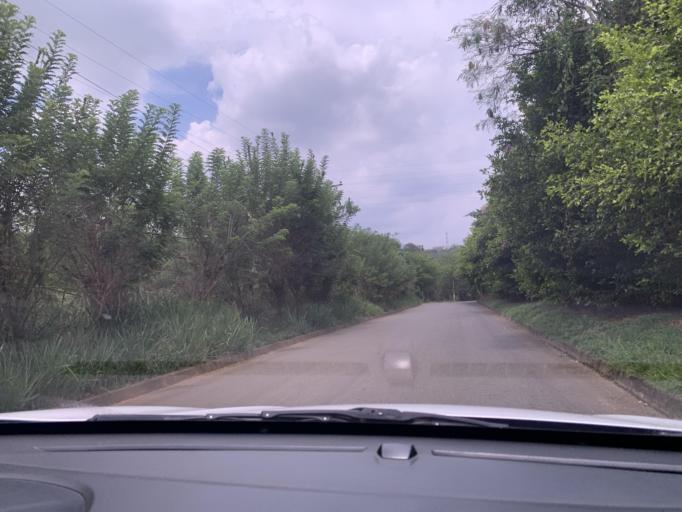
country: CO
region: Valle del Cauca
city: Jamundi
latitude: 3.3369
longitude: -76.5515
